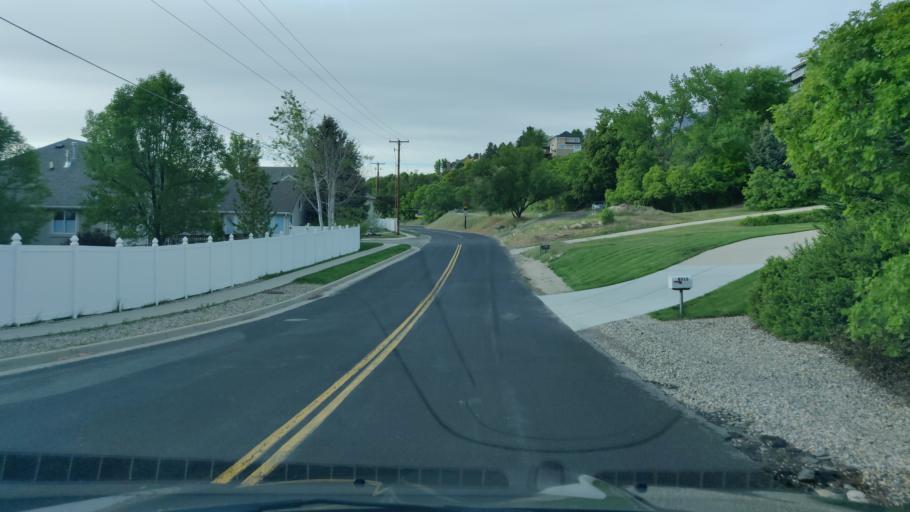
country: US
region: Utah
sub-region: Salt Lake County
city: Granite
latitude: 40.5961
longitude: -111.8007
